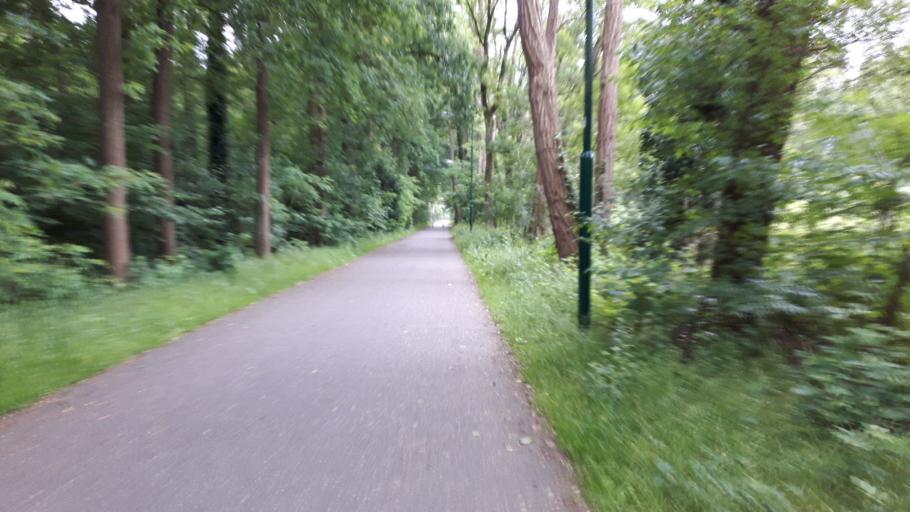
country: NL
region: Utrecht
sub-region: Gemeente De Bilt
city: De Bilt
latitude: 52.1380
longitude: 5.1992
